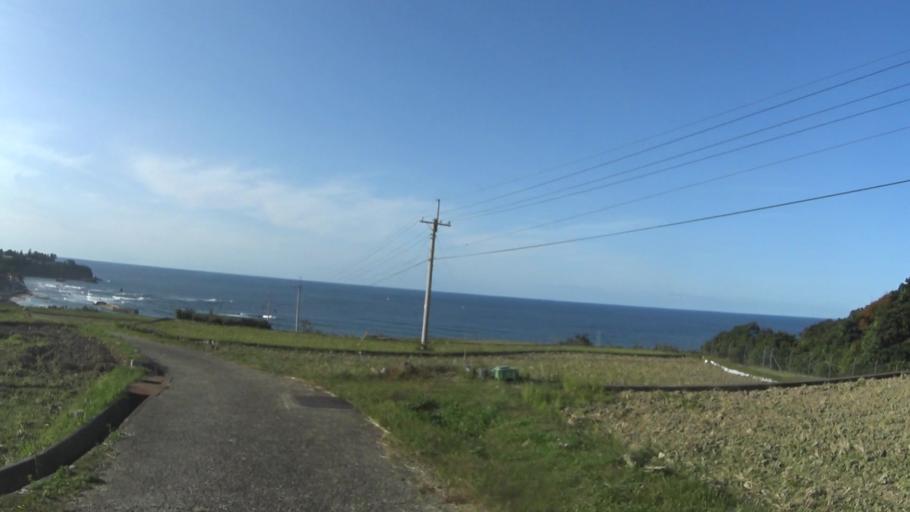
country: JP
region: Kyoto
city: Miyazu
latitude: 35.7625
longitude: 135.2091
